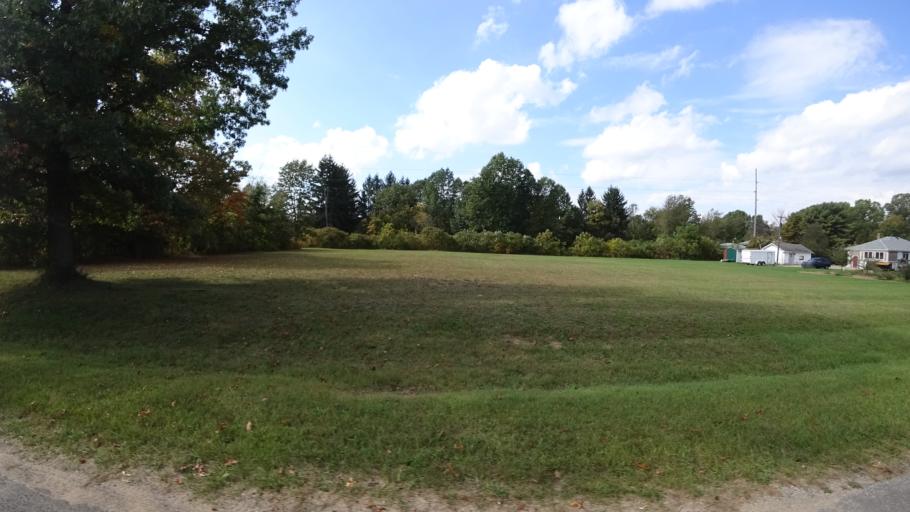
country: US
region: Michigan
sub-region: Saint Joseph County
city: Three Rivers
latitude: 41.9390
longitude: -85.6055
